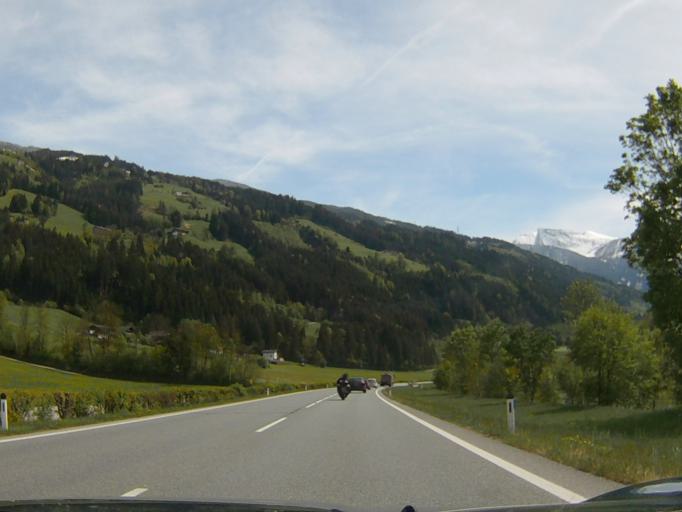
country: AT
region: Tyrol
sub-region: Politischer Bezirk Schwaz
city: Rohrberg
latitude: 47.2579
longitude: 11.9008
